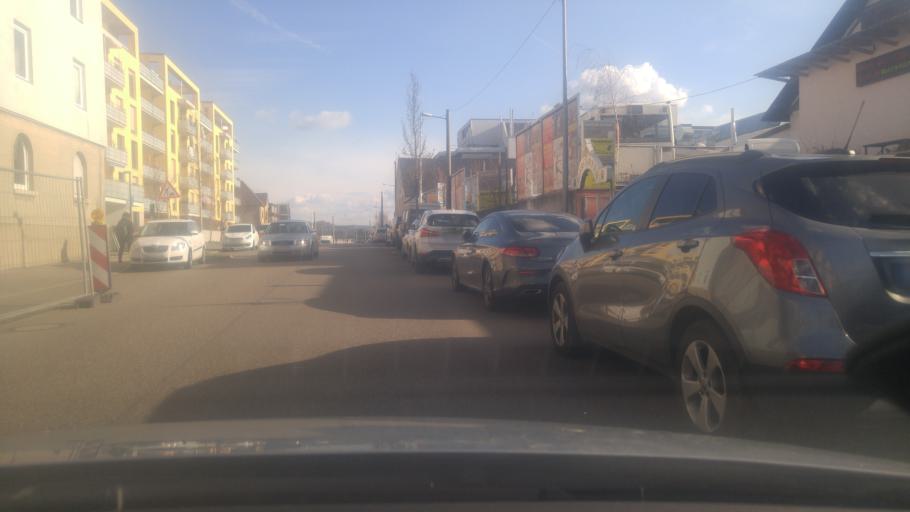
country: DE
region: Baden-Wuerttemberg
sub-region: Regierungsbezirk Stuttgart
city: Stuttgart Feuerbach
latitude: 48.8356
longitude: 9.1636
